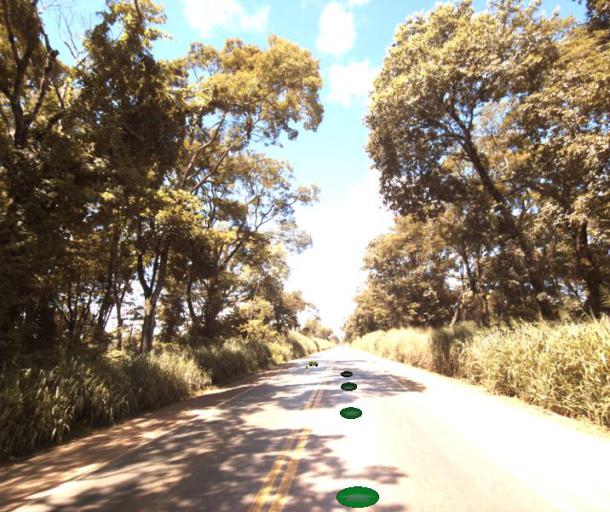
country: BR
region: Goias
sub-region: Anapolis
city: Anapolis
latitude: -16.1448
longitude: -49.0463
